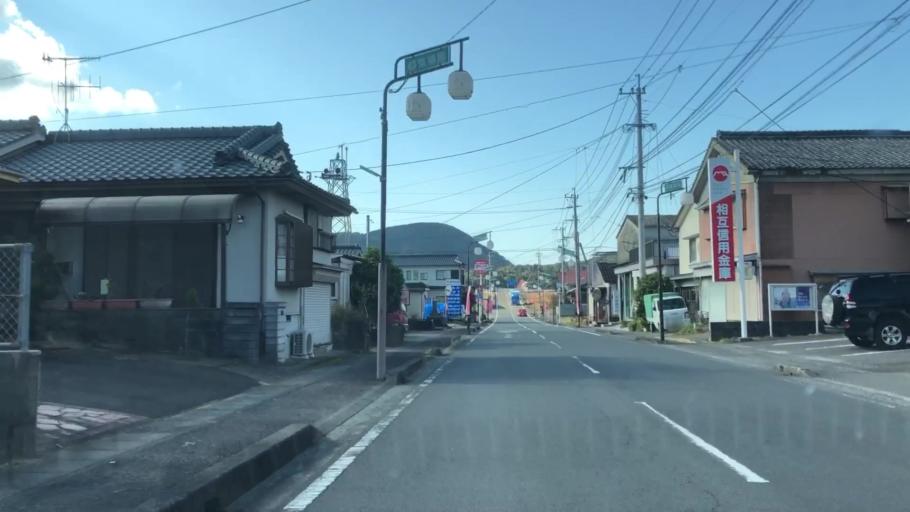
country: JP
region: Kagoshima
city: Satsumasendai
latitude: 31.8640
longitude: 130.3334
